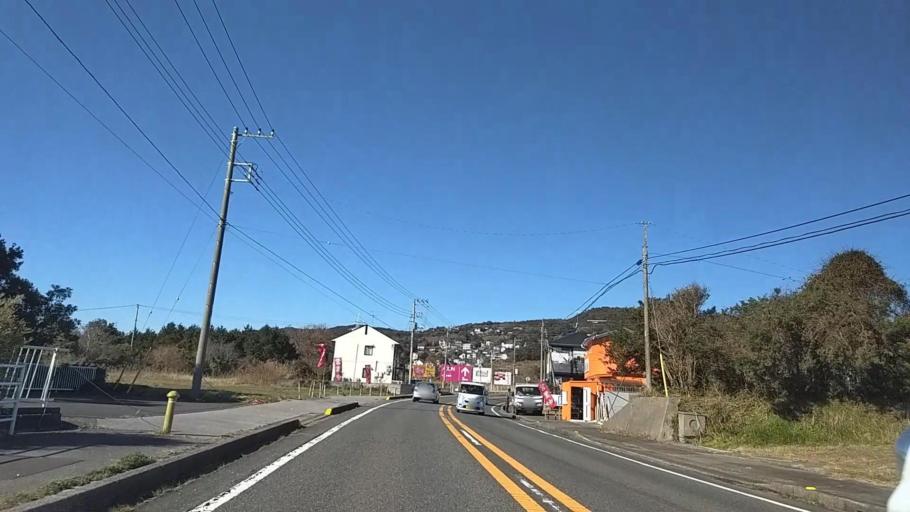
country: JP
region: Chiba
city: Kawaguchi
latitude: 35.0876
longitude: 140.0915
